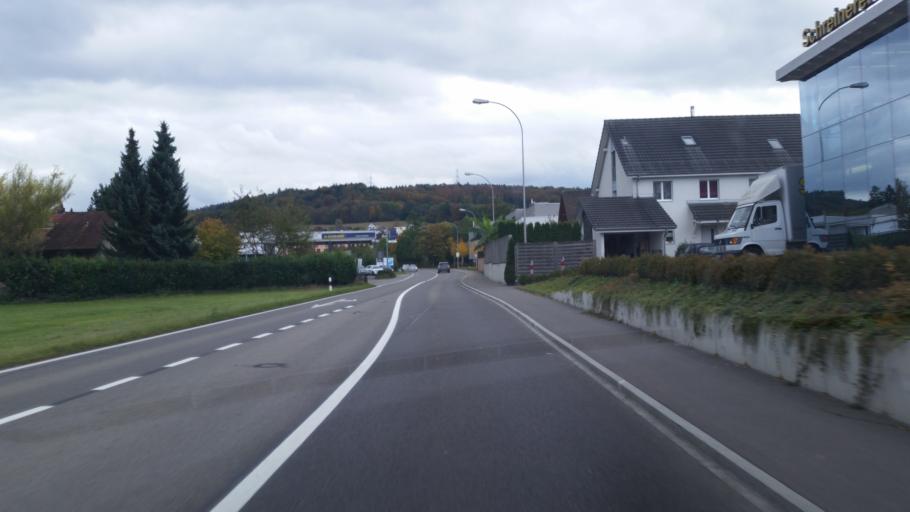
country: CH
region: Aargau
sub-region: Bezirk Zurzach
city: Oberendingen
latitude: 47.5411
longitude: 8.2898
